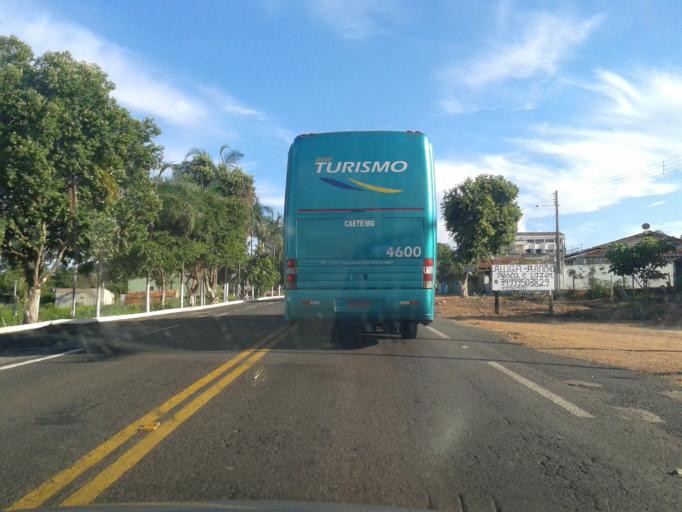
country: BR
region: Minas Gerais
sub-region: Tupaciguara
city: Tupaciguara
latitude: -18.3135
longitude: -48.5621
